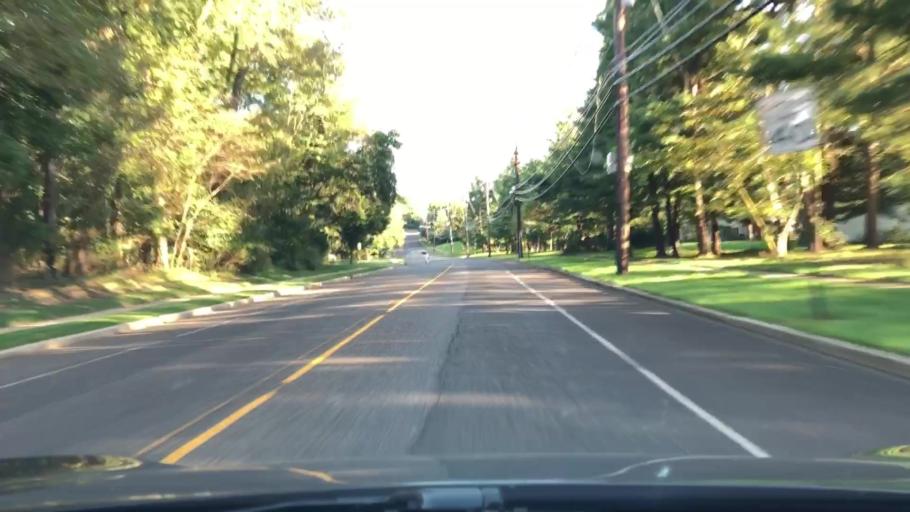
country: US
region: New Jersey
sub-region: Mercer County
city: Lawrenceville
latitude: 40.3097
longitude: -74.7341
